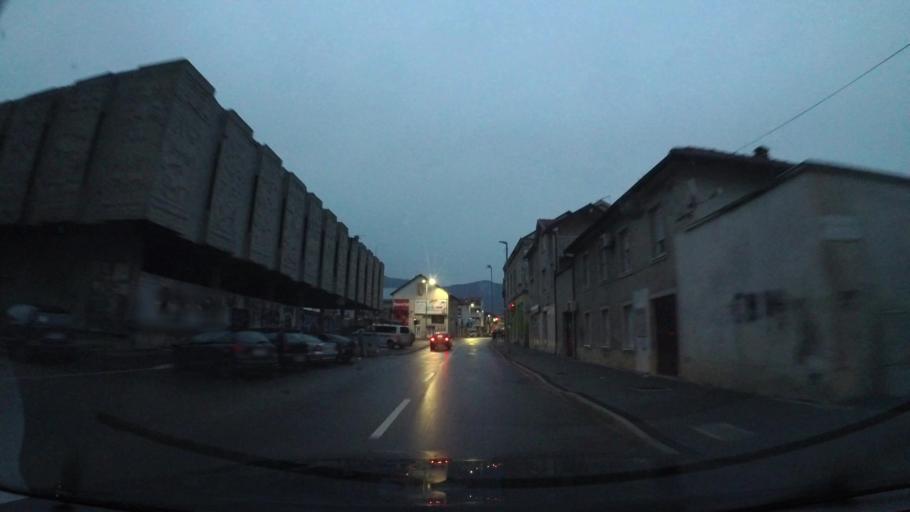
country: BA
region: Federation of Bosnia and Herzegovina
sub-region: Hercegovacko-Bosanski Kanton
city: Mostar
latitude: 43.3437
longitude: 17.8139
